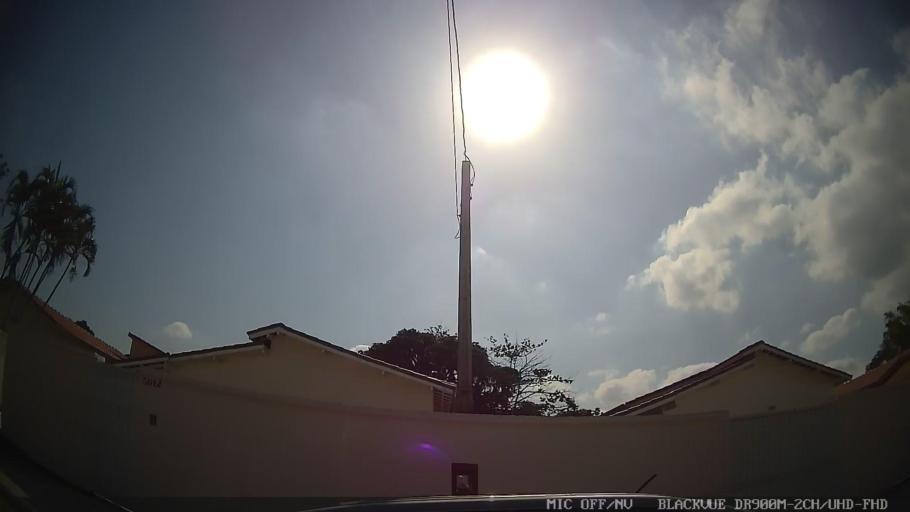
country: BR
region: Sao Paulo
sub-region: Santos
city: Santos
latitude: -23.9389
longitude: -46.2980
